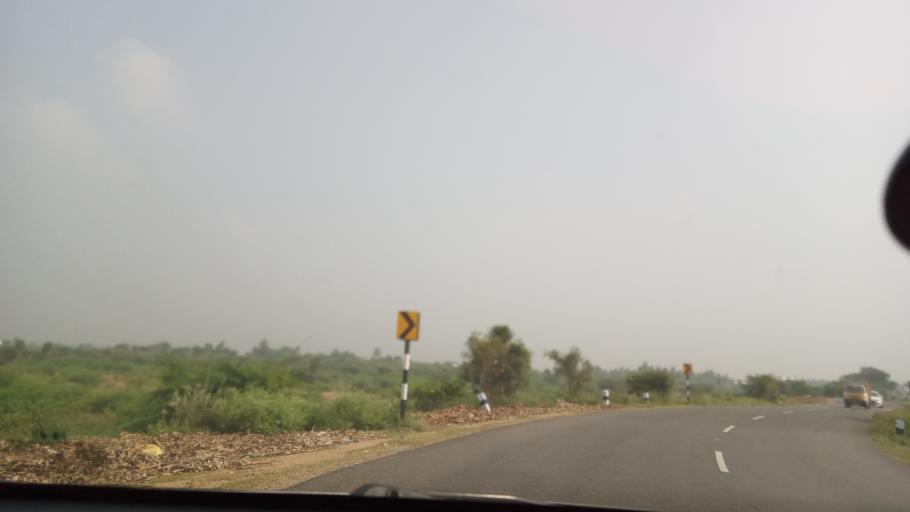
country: IN
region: Tamil Nadu
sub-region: Erode
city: Punjai Puliyampatti
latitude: 11.3940
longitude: 77.1786
